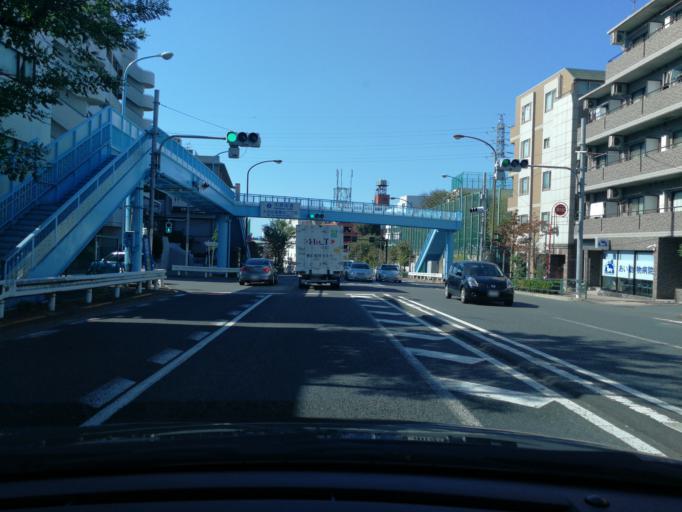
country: JP
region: Kanagawa
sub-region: Kawasaki-shi
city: Kawasaki
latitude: 35.5996
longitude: 139.6875
